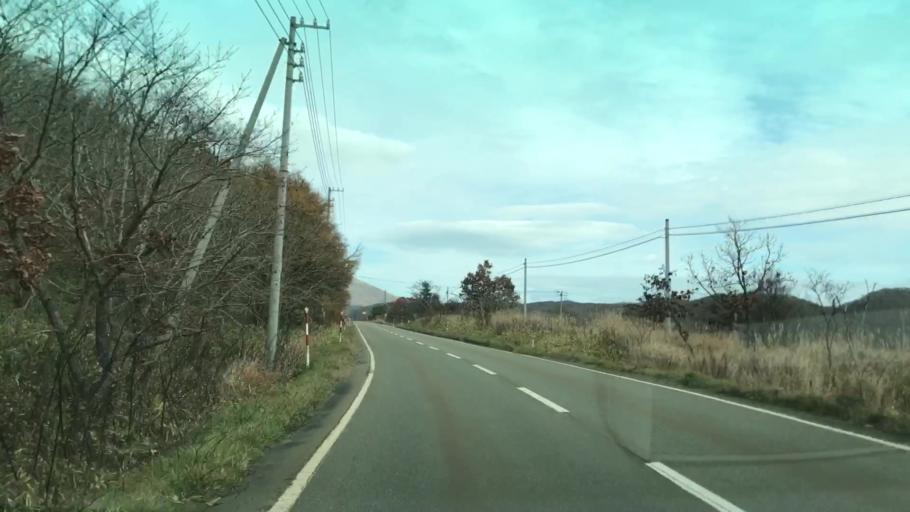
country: JP
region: Hokkaido
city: Shizunai-furukawacho
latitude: 42.0051
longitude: 143.1868
